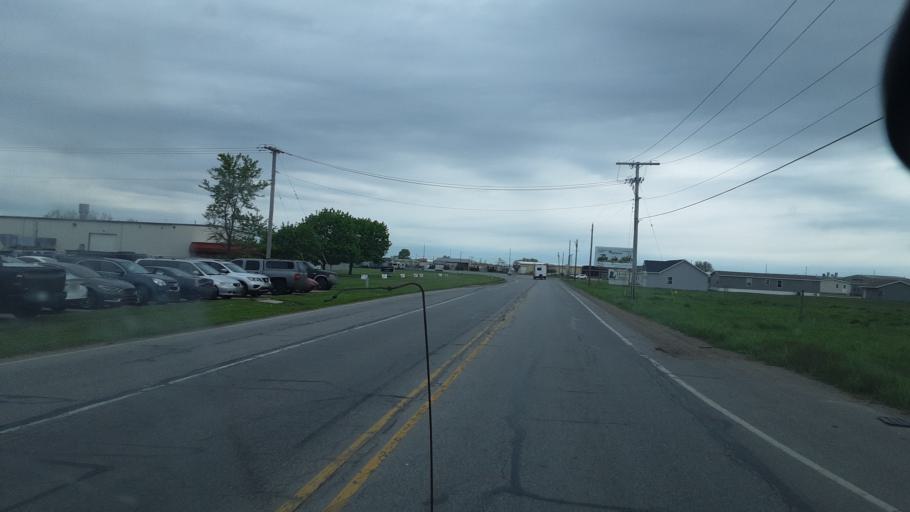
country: US
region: Indiana
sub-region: Elkhart County
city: Goshen
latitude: 41.5459
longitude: -85.7801
